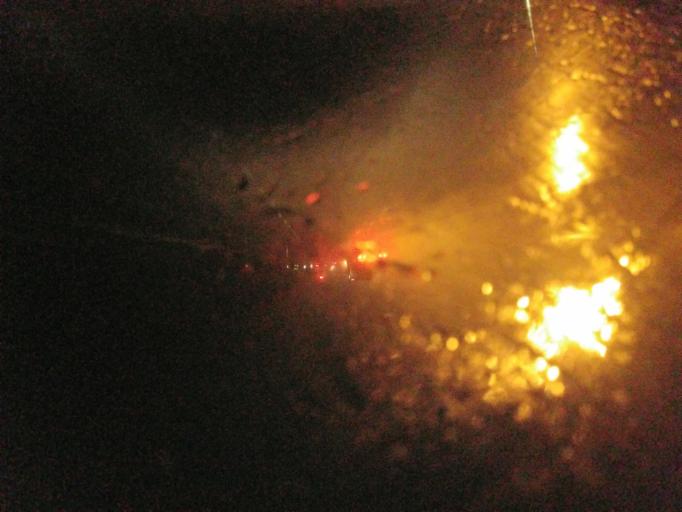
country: US
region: Illinois
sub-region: Fayette County
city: Vandalia
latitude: 38.9746
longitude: -89.0080
